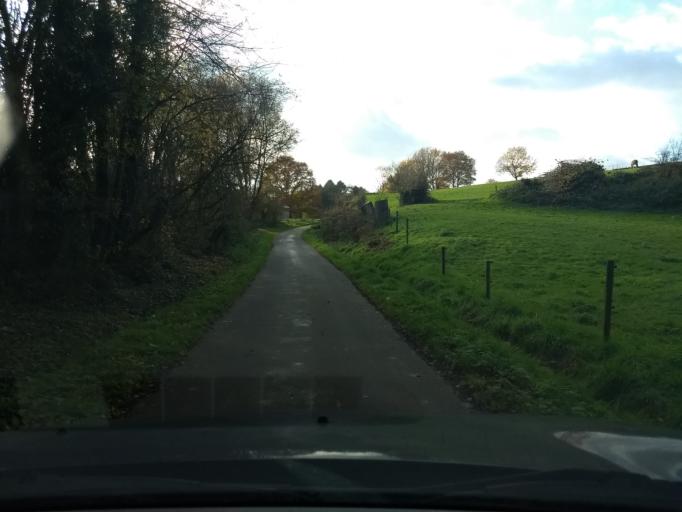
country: BE
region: Wallonia
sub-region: Province du Brabant Wallon
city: Ittre
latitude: 50.5987
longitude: 4.2799
